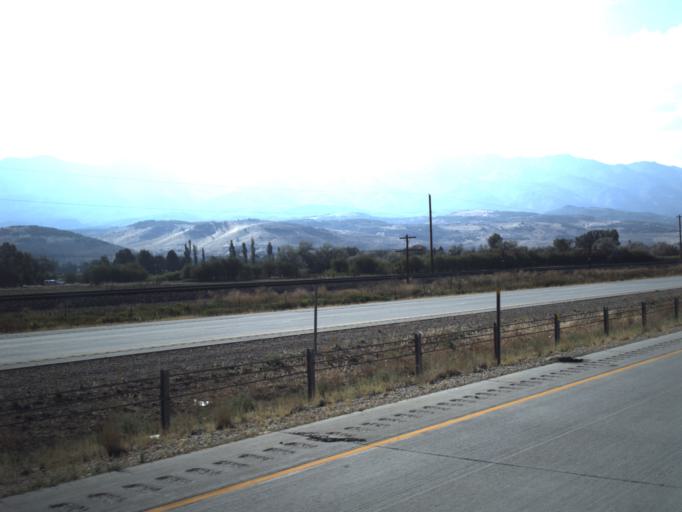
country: US
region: Utah
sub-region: Morgan County
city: Morgan
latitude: 41.0616
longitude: -111.7041
